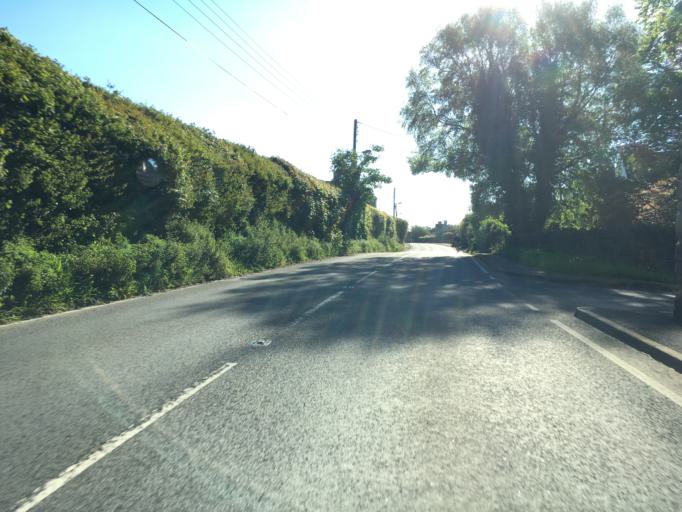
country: GB
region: England
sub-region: North Somerset
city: Clevedon
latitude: 51.4413
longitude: -2.8184
